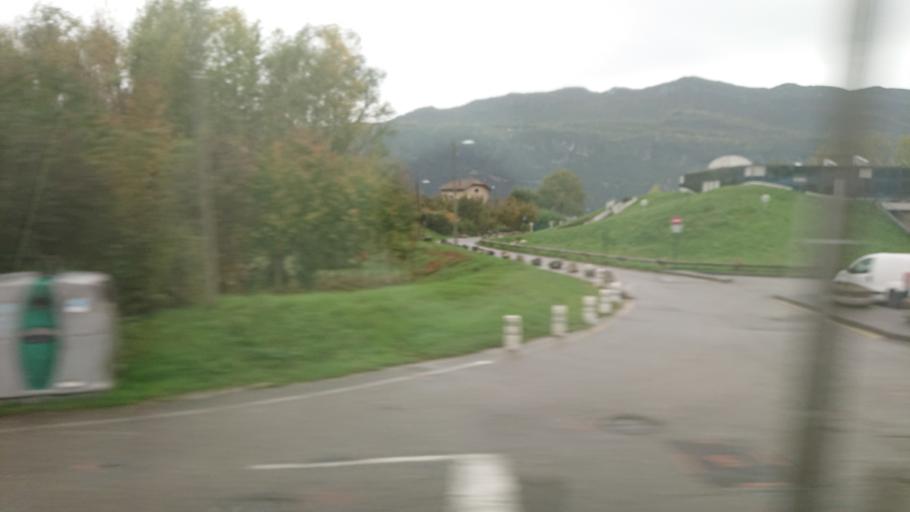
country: FR
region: Rhone-Alpes
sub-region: Departement de la Savoie
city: Brison-Saint-Innocent
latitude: 45.7090
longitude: 5.8920
